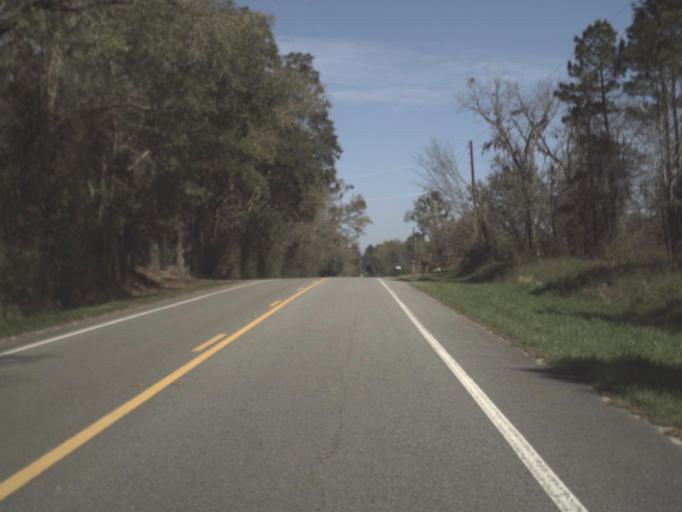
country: US
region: Florida
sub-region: Jefferson County
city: Monticello
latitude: 30.5139
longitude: -84.0243
